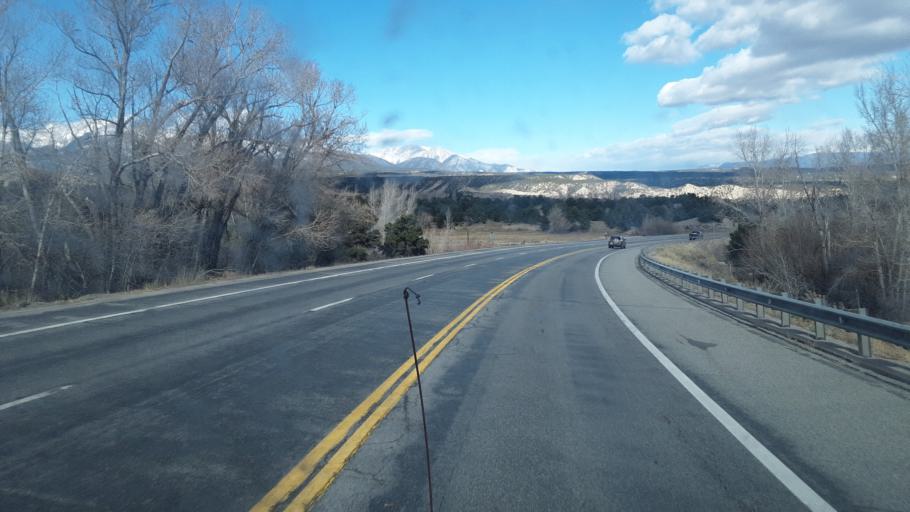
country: US
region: Colorado
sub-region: Chaffee County
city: Salida
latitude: 38.5529
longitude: -106.0828
